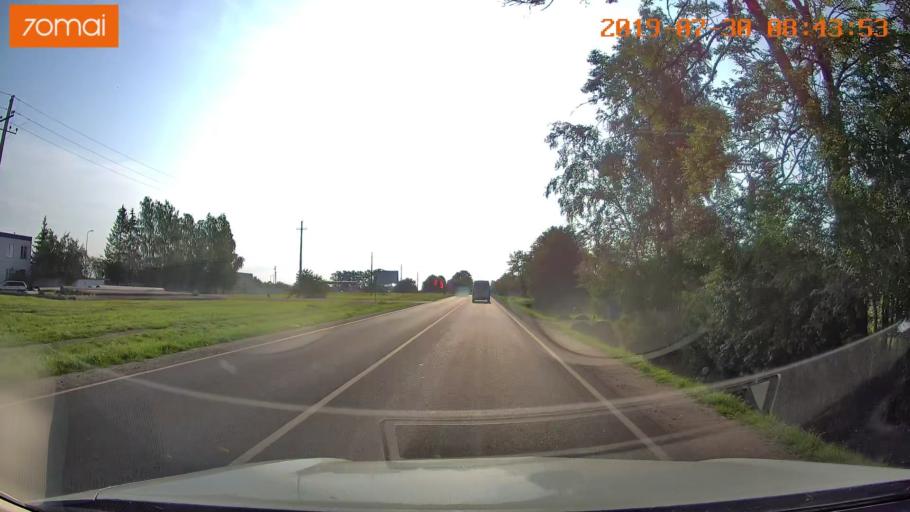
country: RU
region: Kaliningrad
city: Chernyakhovsk
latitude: 54.6267
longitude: 21.8485
